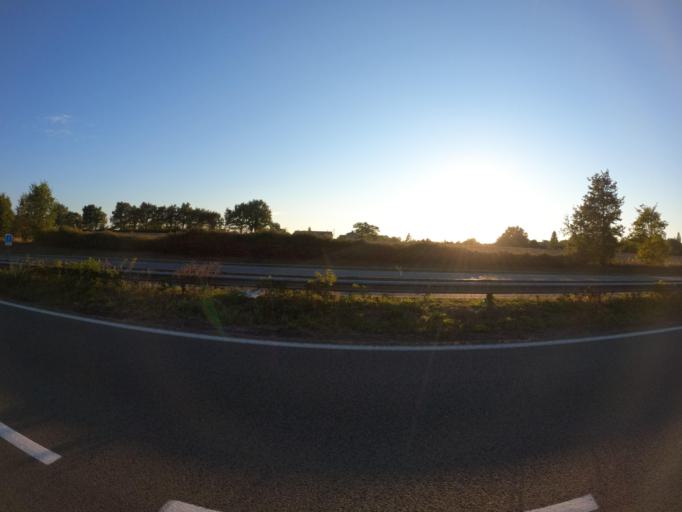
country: FR
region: Pays de la Loire
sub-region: Departement de la Vendee
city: Bournezeau
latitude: 46.6326
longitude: -1.1792
